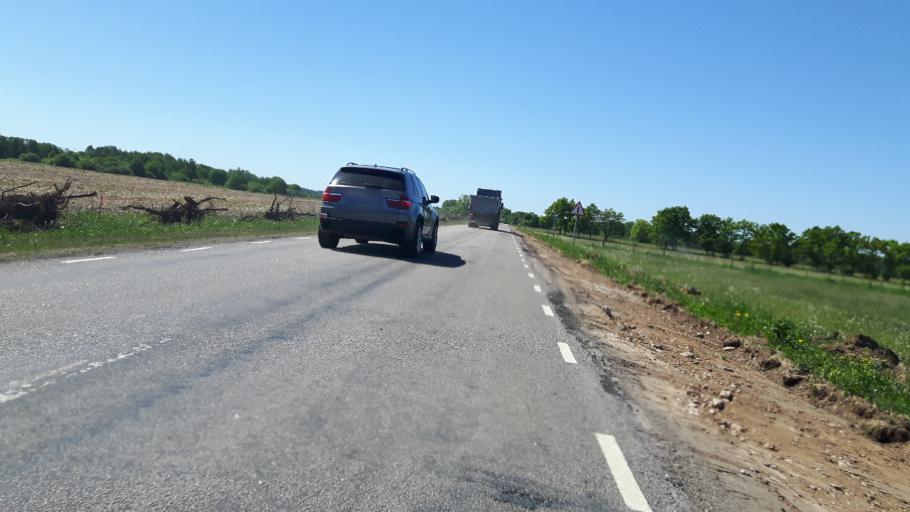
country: EE
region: Ida-Virumaa
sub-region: Narva-Joesuu linn
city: Narva-Joesuu
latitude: 59.3983
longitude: 27.9313
